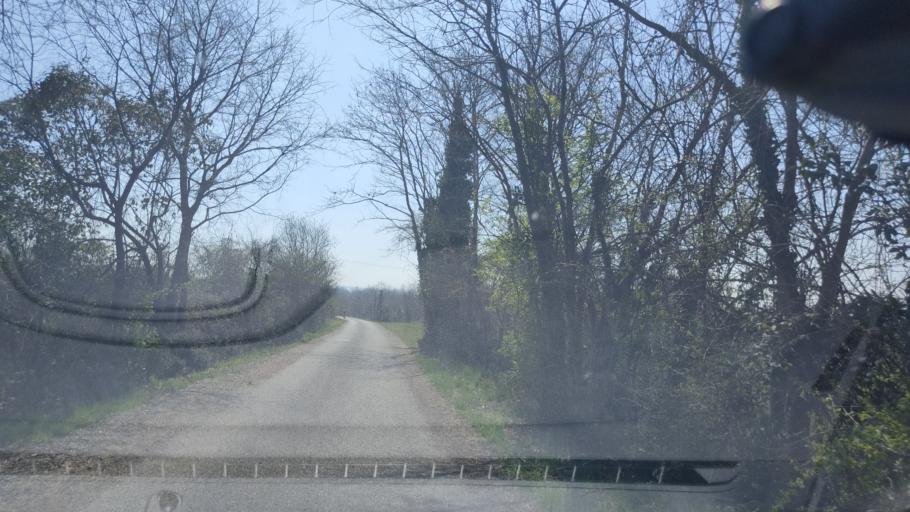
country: IT
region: Friuli Venezia Giulia
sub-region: Provincia di Pordenone
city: Budoia
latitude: 46.0346
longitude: 12.5403
